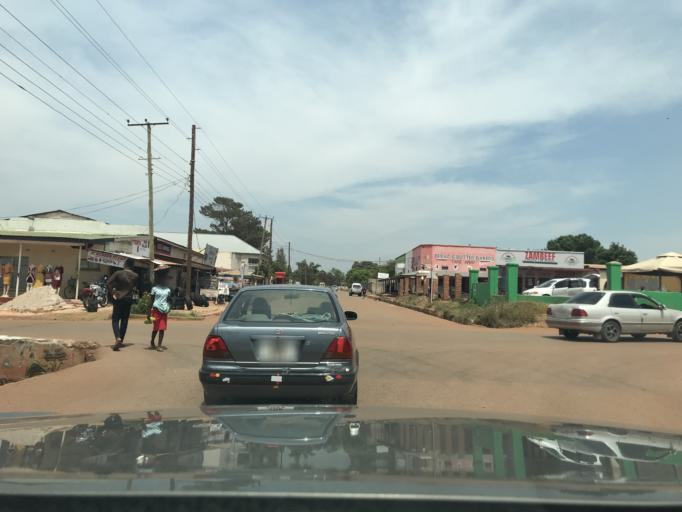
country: ZM
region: Northern
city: Kasama
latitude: -10.2043
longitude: 31.1881
